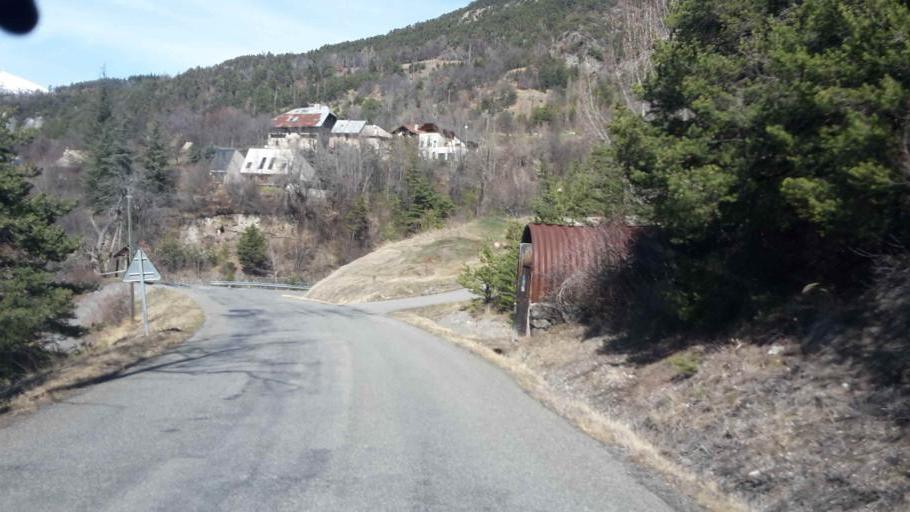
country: FR
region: Provence-Alpes-Cote d'Azur
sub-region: Departement des Hautes-Alpes
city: Embrun
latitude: 44.5629
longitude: 6.5502
